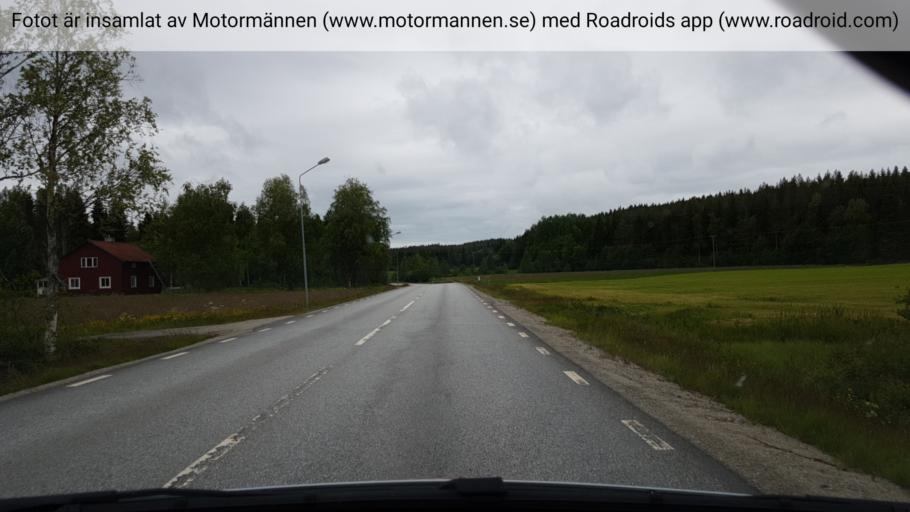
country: SE
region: Vaesterbotten
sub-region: Vindelns Kommun
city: Vindeln
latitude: 64.1210
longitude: 19.5617
